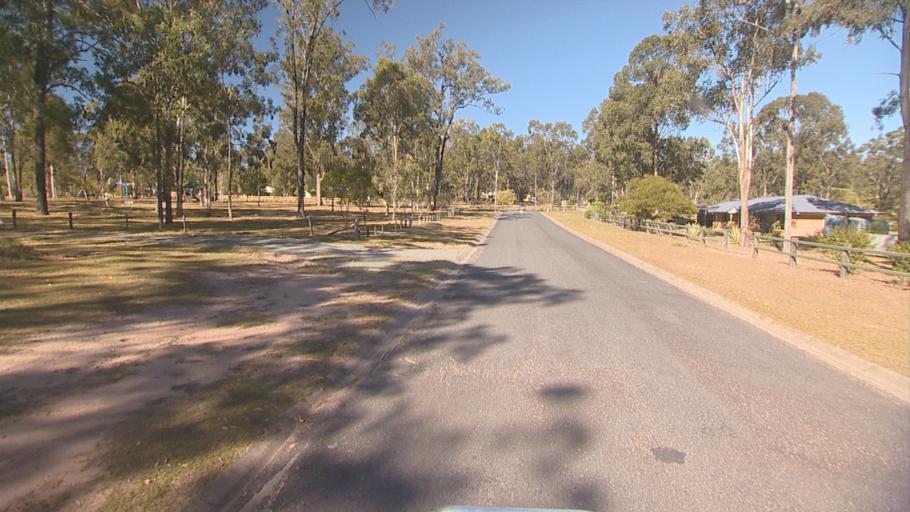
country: AU
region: Queensland
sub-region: Logan
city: North Maclean
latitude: -27.8259
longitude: 152.9441
